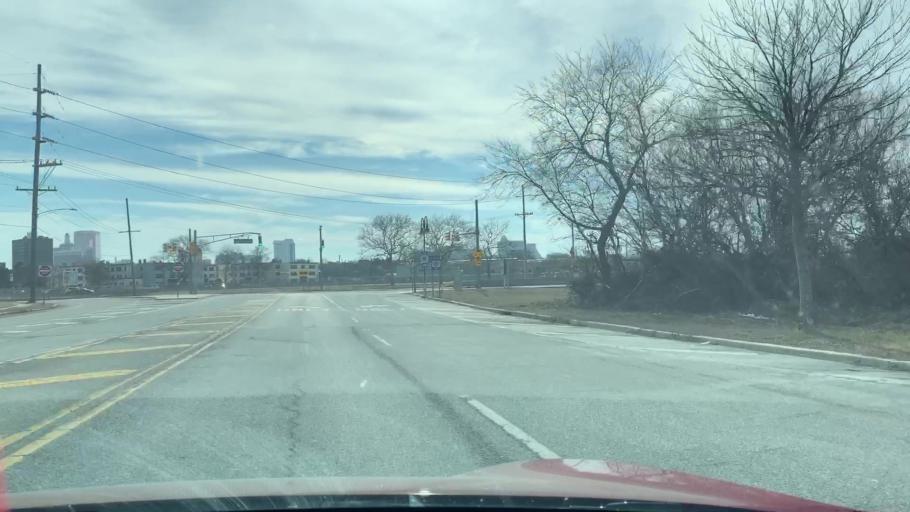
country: US
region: New Jersey
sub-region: Atlantic County
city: Atlantic City
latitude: 39.3729
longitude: -74.4322
